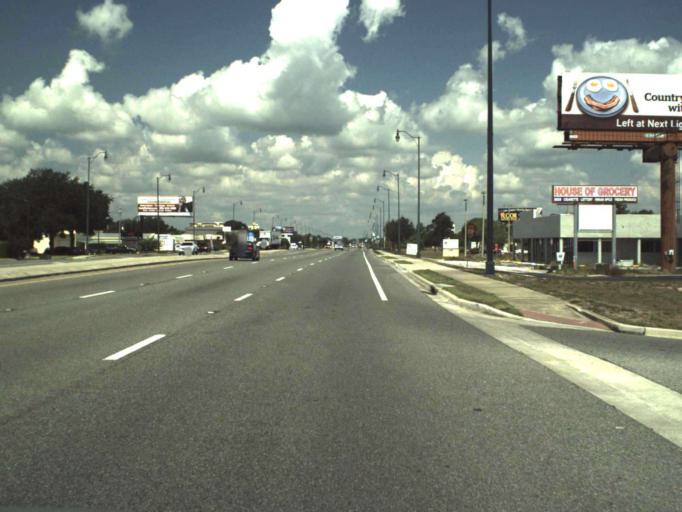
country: US
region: Florida
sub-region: Lake County
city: Silver Lake
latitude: 28.8240
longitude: -81.7891
